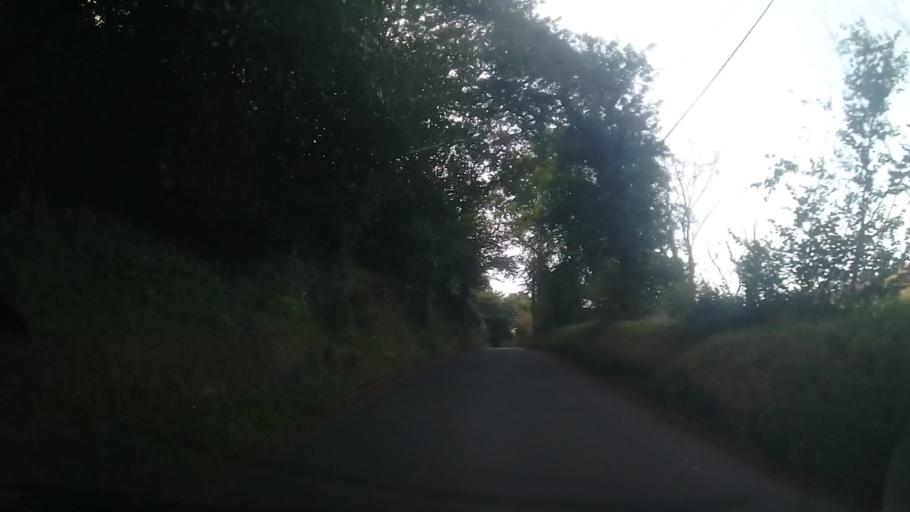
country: GB
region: Wales
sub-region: Pembrokeshire
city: Fishguard
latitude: 51.9812
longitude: -4.9354
